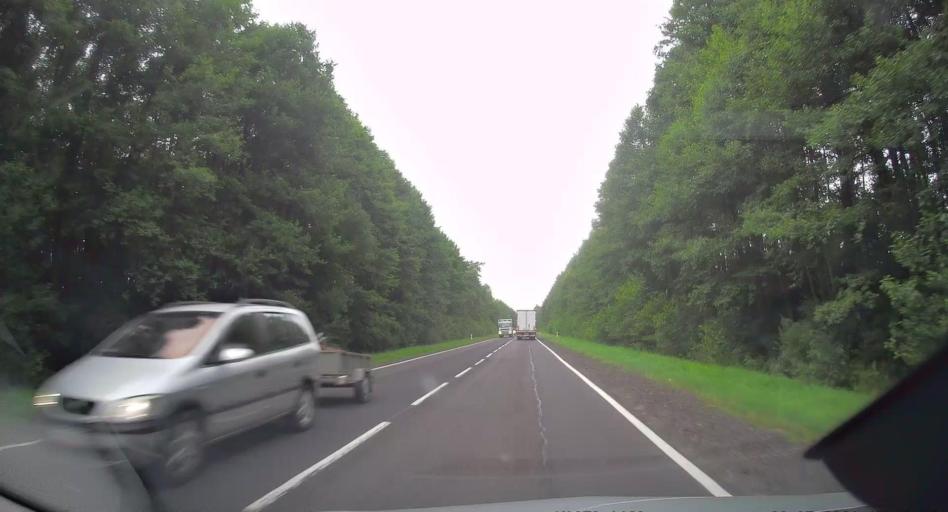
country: PL
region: Lodz Voivodeship
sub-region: Powiat radomszczanski
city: Radomsko
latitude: 51.0249
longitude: 19.4338
